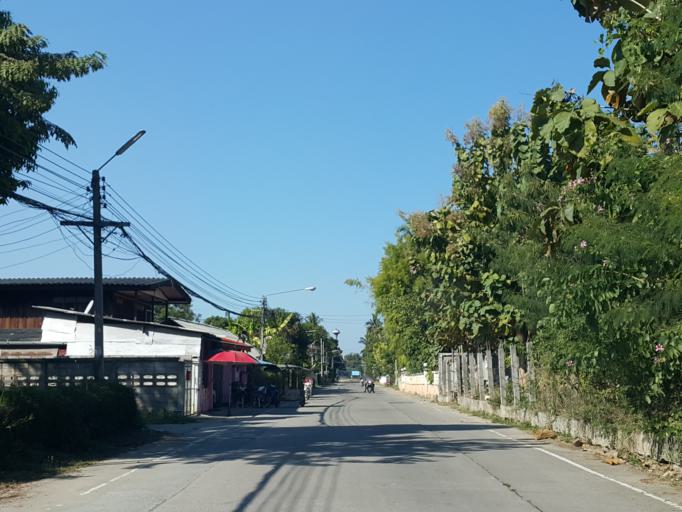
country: TH
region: Chiang Mai
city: San Sai
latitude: 18.8827
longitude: 99.0123
